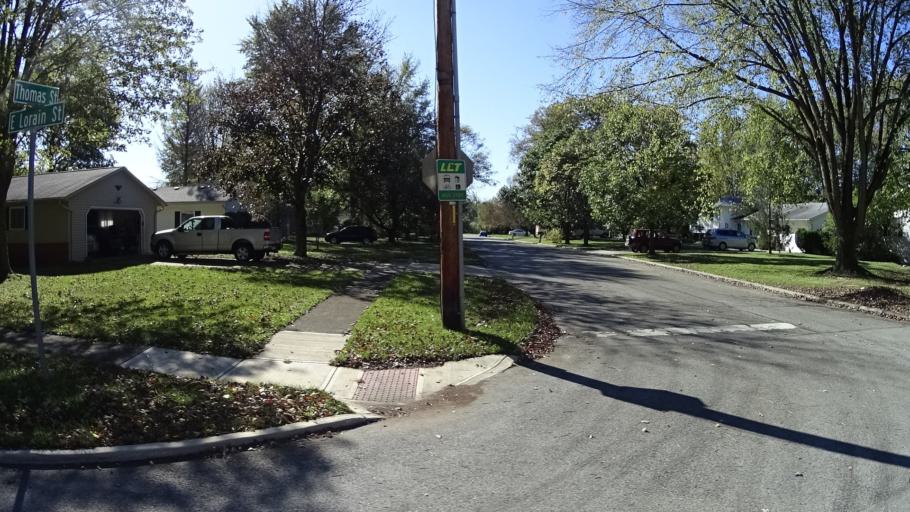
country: US
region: Ohio
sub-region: Lorain County
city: Oberlin
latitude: 41.2939
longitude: -82.1956
